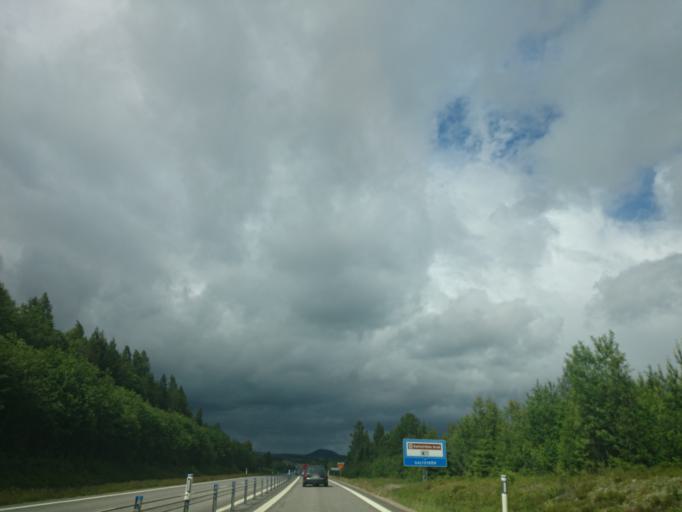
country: SE
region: Vaesternorrland
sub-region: Sundsvalls Kommun
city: Njurundabommen
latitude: 62.2375
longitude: 17.3750
